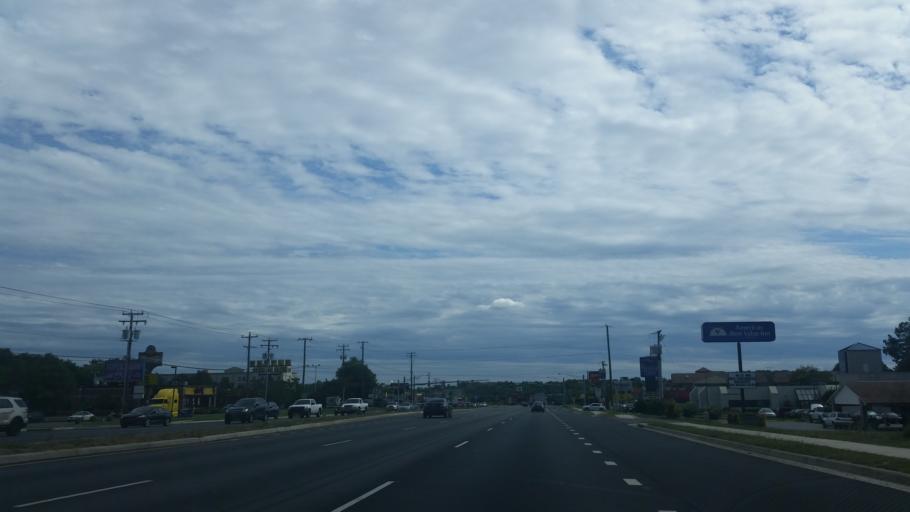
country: US
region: Virginia
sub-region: Stafford County
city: Falmouth
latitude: 38.3466
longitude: -77.5003
